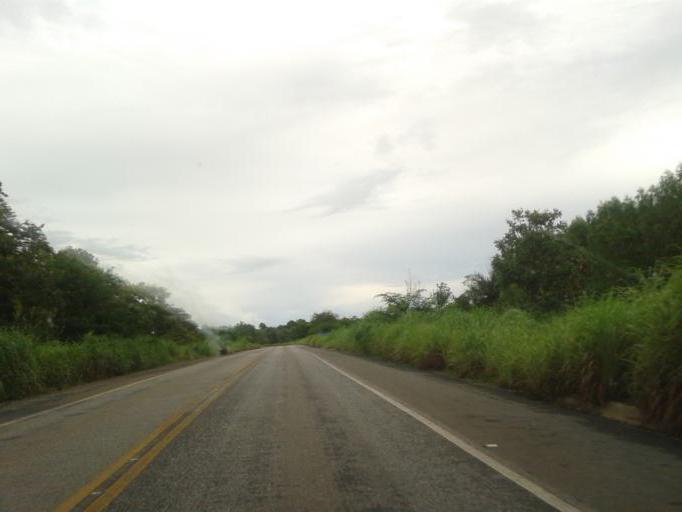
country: BR
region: Goias
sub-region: Mozarlandia
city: Mozarlandia
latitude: -14.8263
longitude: -50.5328
